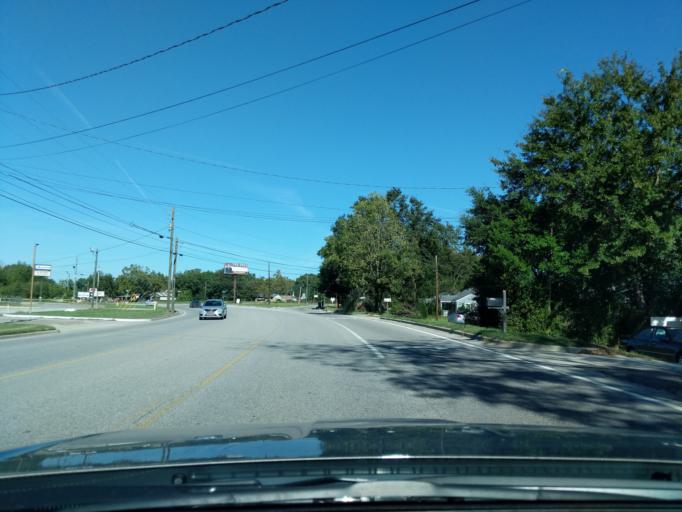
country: US
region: Georgia
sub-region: Richmond County
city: Augusta
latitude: 33.4290
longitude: -82.0061
